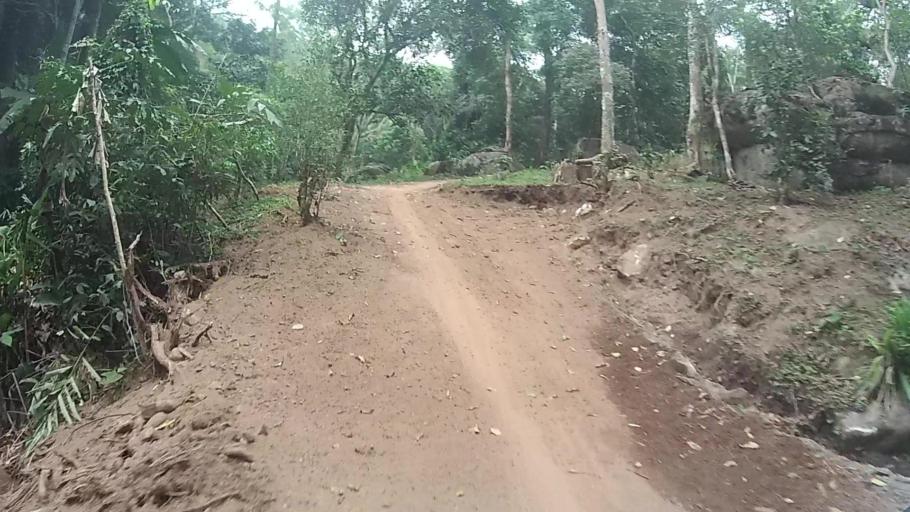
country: TH
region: Lampang
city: Mueang Pan
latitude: 18.8348
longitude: 99.3928
